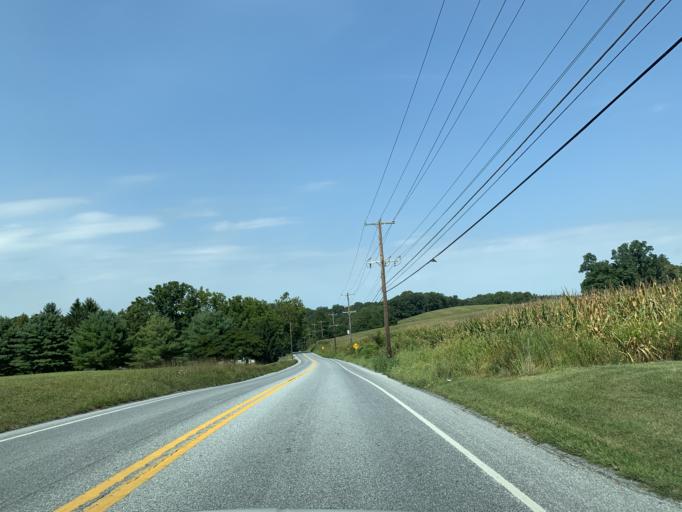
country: US
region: Pennsylvania
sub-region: York County
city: Susquehanna Trails
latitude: 39.7601
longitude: -76.3284
